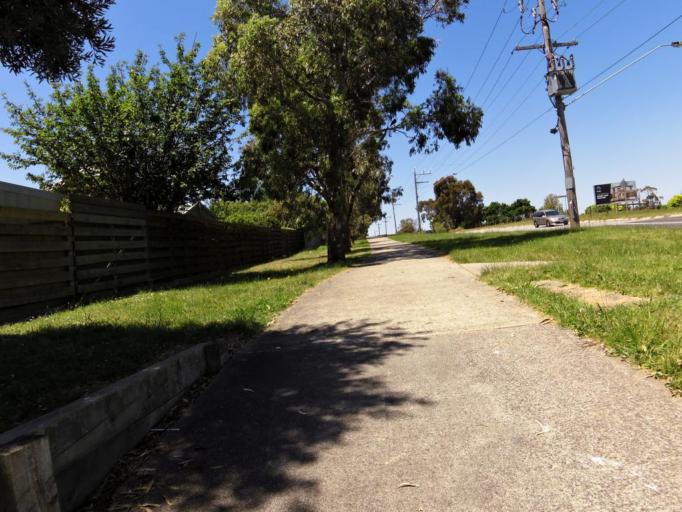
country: AU
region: Victoria
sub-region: Casey
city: Berwick
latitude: -38.0607
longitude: 145.3438
